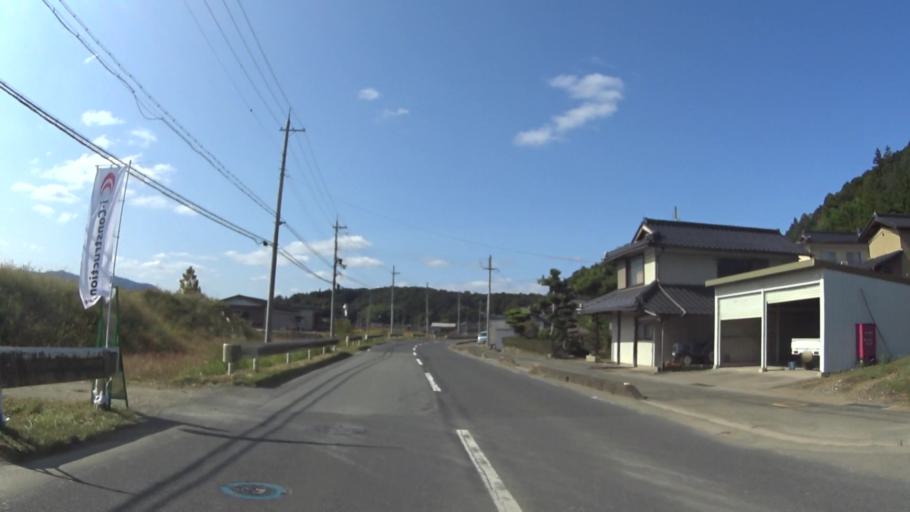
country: JP
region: Kyoto
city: Fukuchiyama
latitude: 35.3124
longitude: 135.1626
